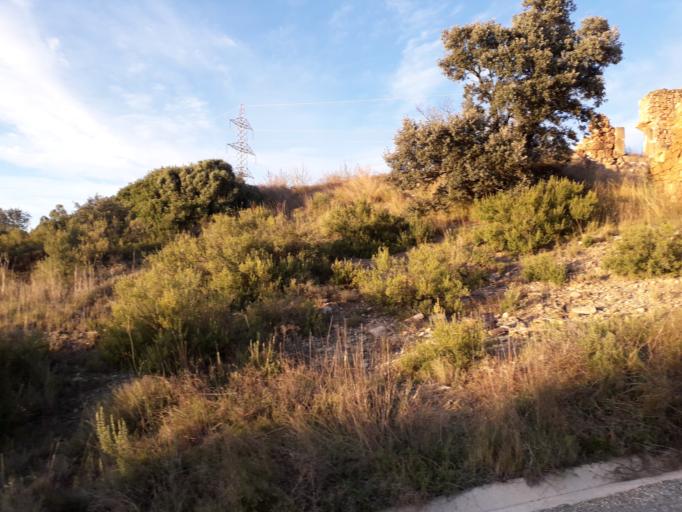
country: ES
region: Catalonia
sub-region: Provincia de Barcelona
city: Jorba
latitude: 41.6245
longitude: 1.5724
